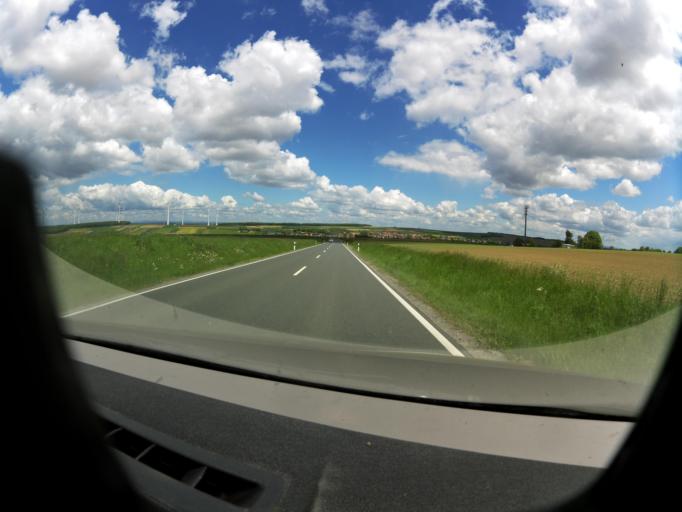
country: DE
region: Bavaria
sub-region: Regierungsbezirk Unterfranken
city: Schwanfeld
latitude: 49.9092
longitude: 10.1311
